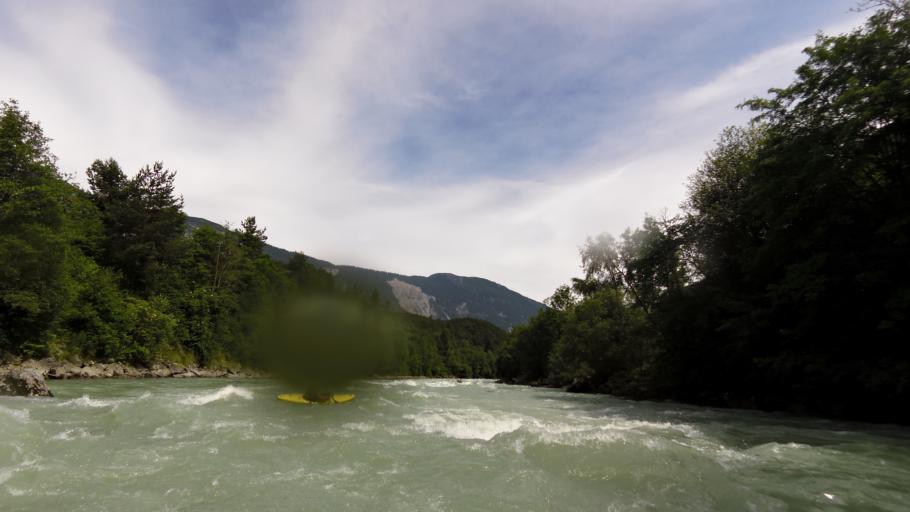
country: AT
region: Tyrol
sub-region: Politischer Bezirk Imst
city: Sautens
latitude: 47.2193
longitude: 10.8568
